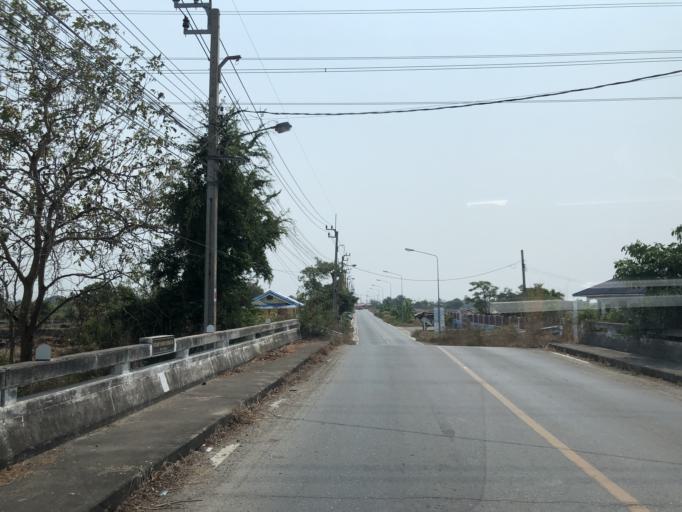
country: TH
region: Samut Prakan
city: Bang Bo
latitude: 13.5476
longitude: 100.8761
